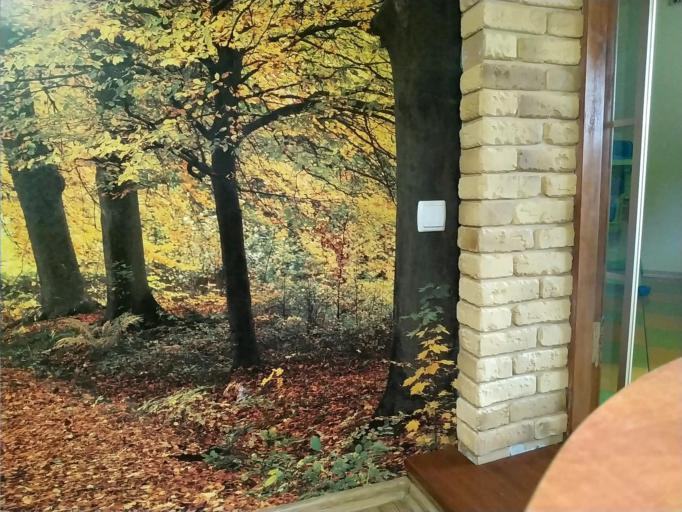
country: RU
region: Smolensk
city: Dorogobuzh
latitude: 54.9368
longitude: 33.3170
